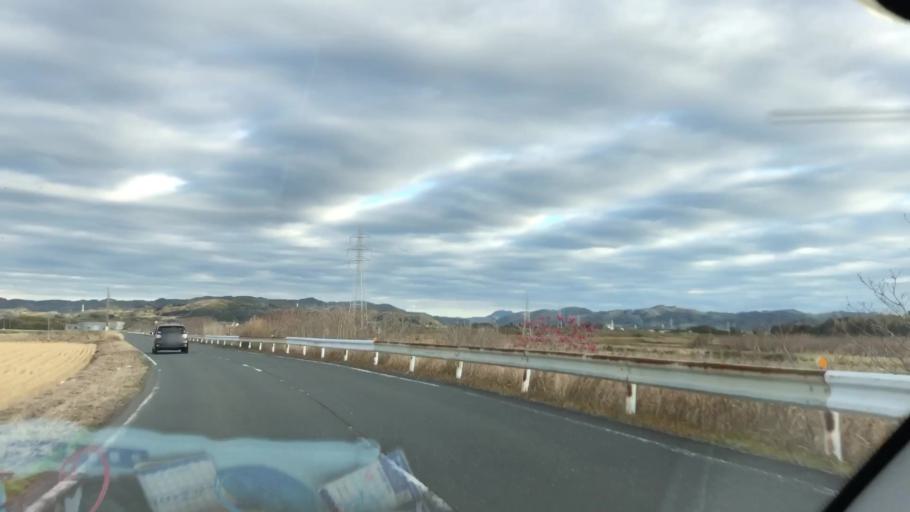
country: JP
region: Chiba
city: Tateyama
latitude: 35.0011
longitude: 139.8846
